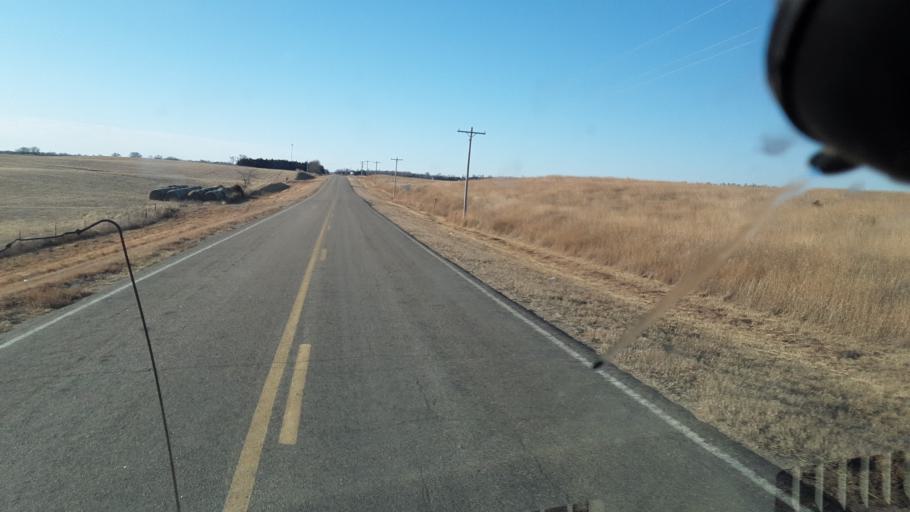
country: US
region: Kansas
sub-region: Barton County
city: Ellinwood
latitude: 38.3114
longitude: -98.6642
